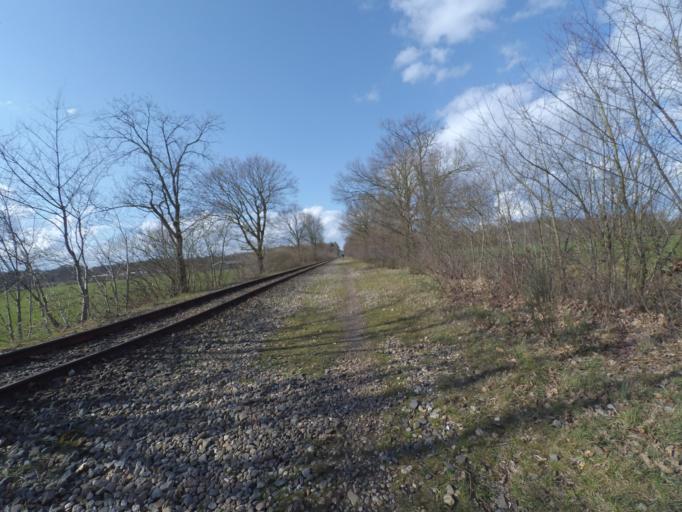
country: NL
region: Utrecht
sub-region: Gemeente Amersfoort
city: Randenbroek
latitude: 52.1286
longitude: 5.4067
